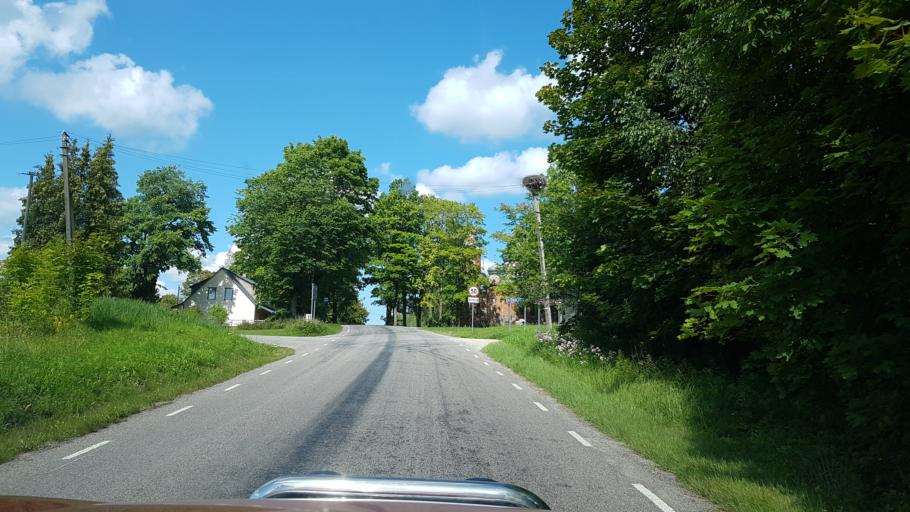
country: EE
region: Vorumaa
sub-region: Voru linn
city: Voru
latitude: 57.6718
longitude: 27.0823
